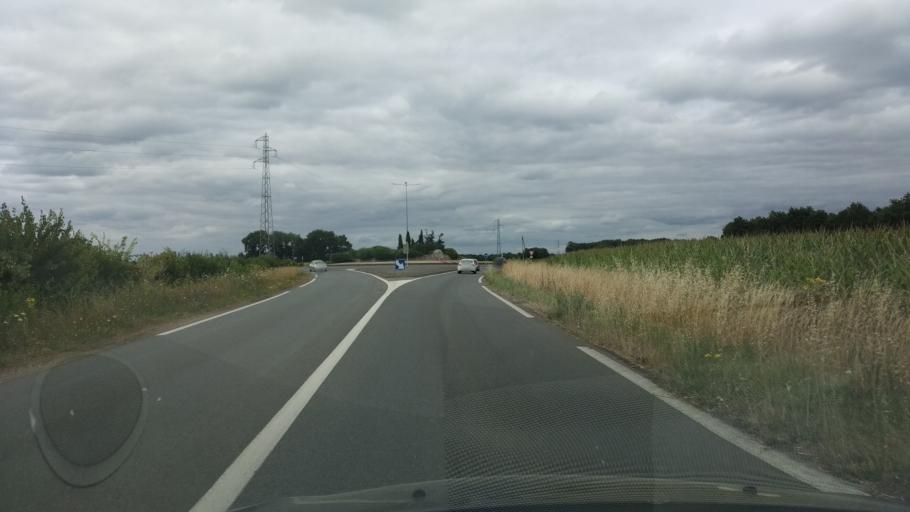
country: FR
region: Poitou-Charentes
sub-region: Departement de la Vienne
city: Smarves
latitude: 46.5171
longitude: 0.3571
